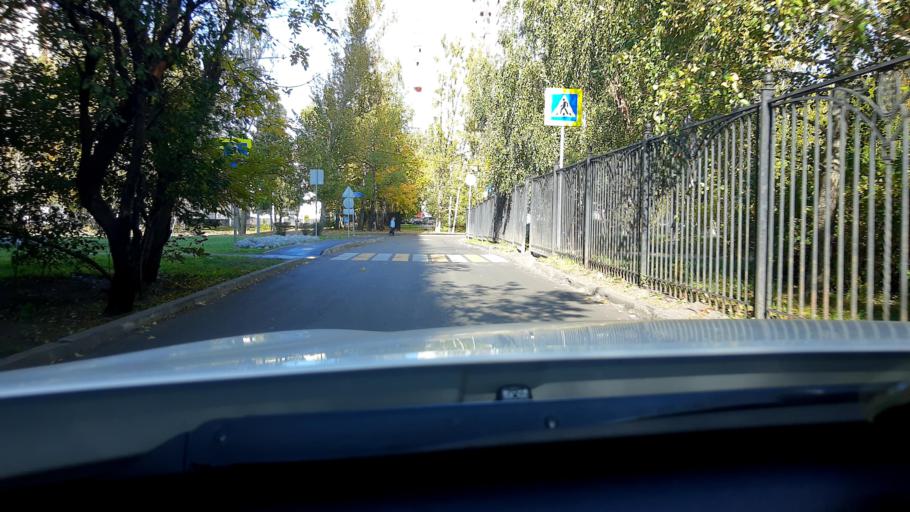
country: RU
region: Moskovskaya
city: Vostochnoe Degunino
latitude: 55.8906
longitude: 37.5632
